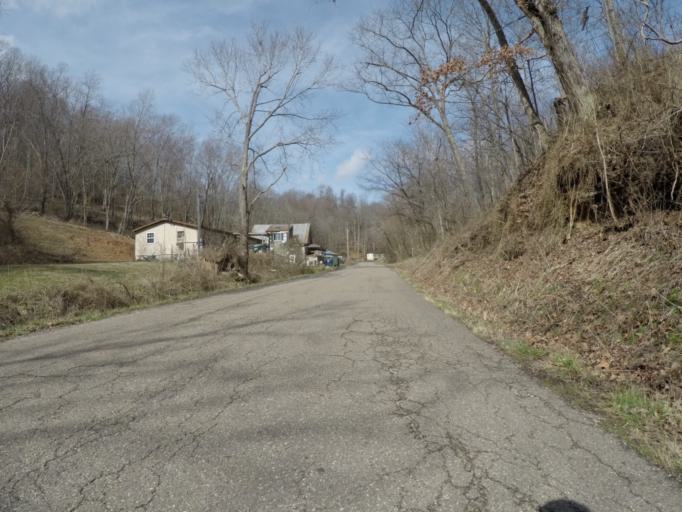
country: US
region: Ohio
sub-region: Lawrence County
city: Burlington
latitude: 38.4814
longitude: -82.5324
